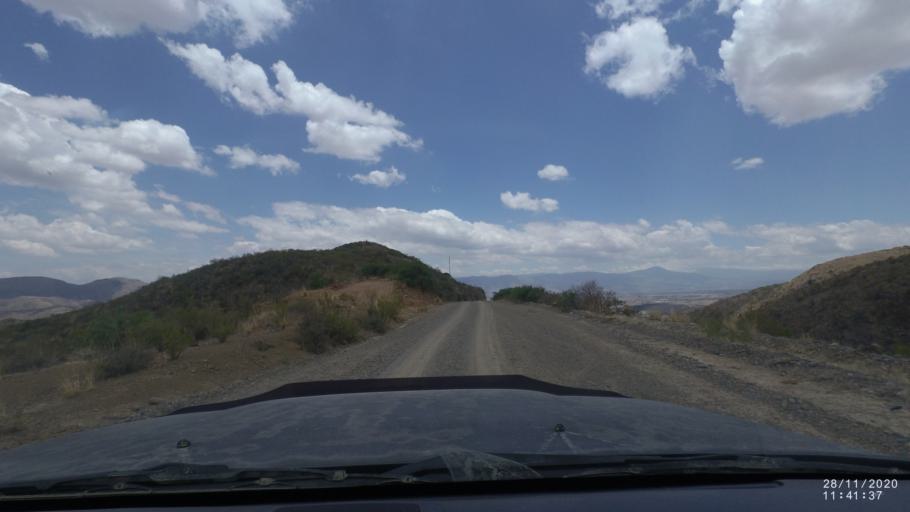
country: BO
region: Cochabamba
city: Tarata
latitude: -17.6690
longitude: -66.0483
